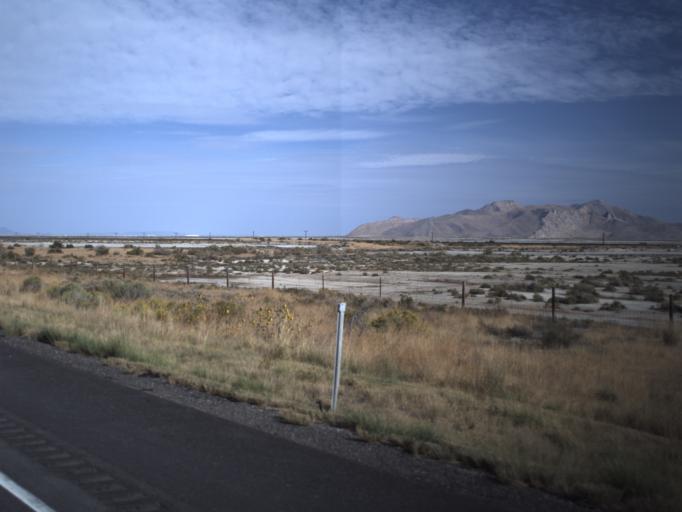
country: US
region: Utah
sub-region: Tooele County
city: Grantsville
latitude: 40.6909
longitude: -112.4616
